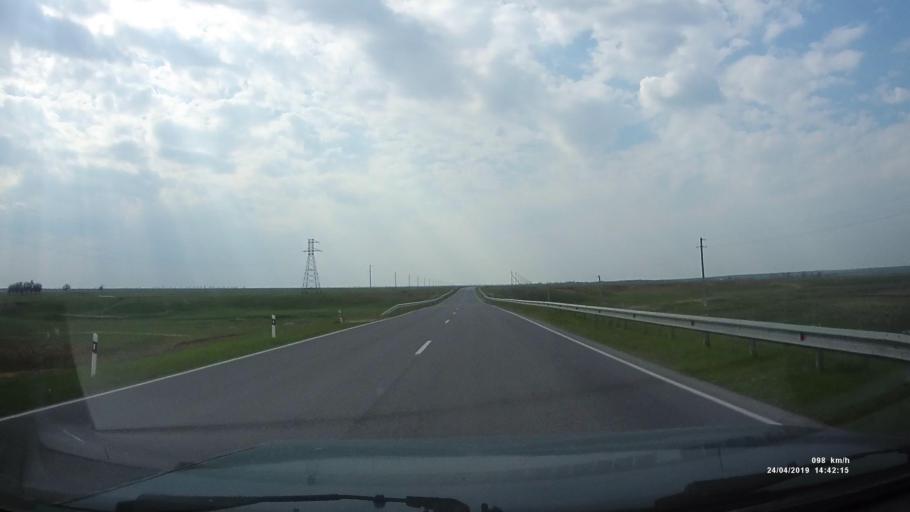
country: RU
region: Rostov
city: Remontnoye
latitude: 46.4511
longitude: 43.8658
